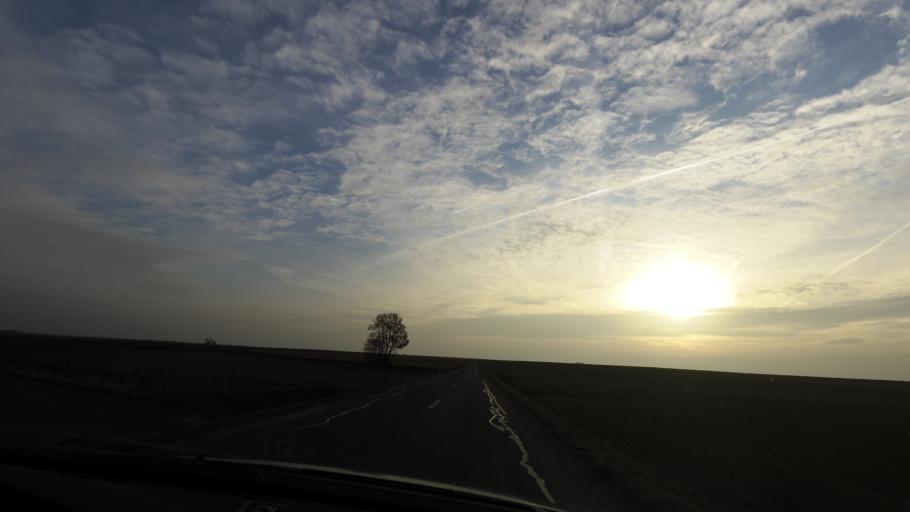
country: NL
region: Limburg
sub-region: Gemeente Nuth
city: Nuth
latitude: 50.9197
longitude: 5.8398
